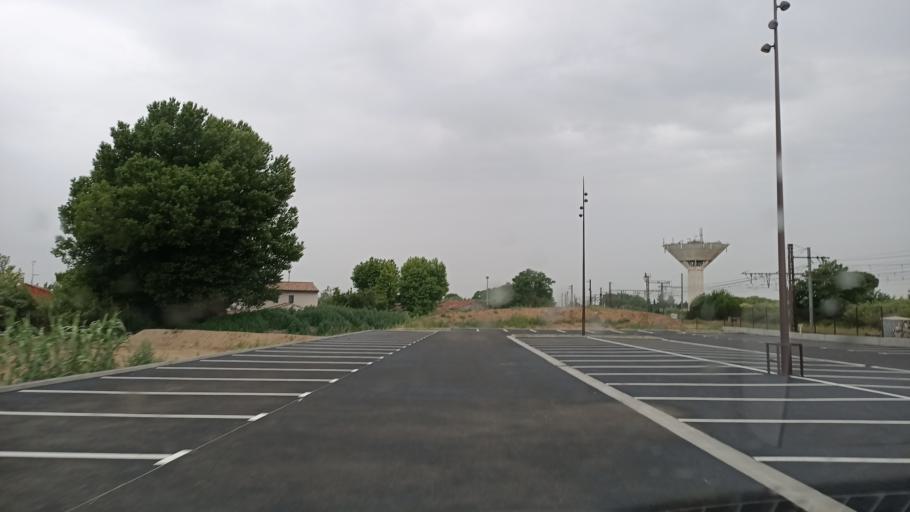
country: FR
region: Languedoc-Roussillon
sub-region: Departement de l'Herault
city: Lunel
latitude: 43.6788
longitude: 4.1254
